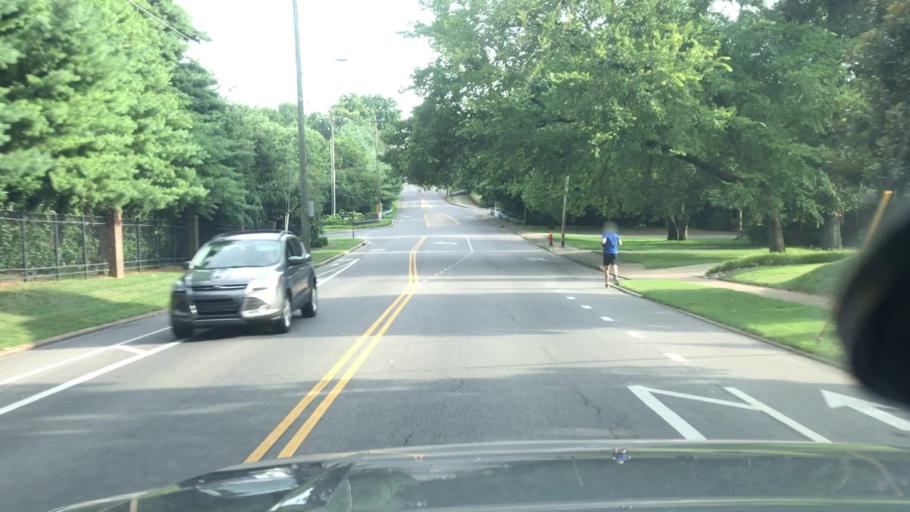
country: US
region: Tennessee
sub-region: Davidson County
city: Belle Meade
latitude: 36.1296
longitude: -86.8260
